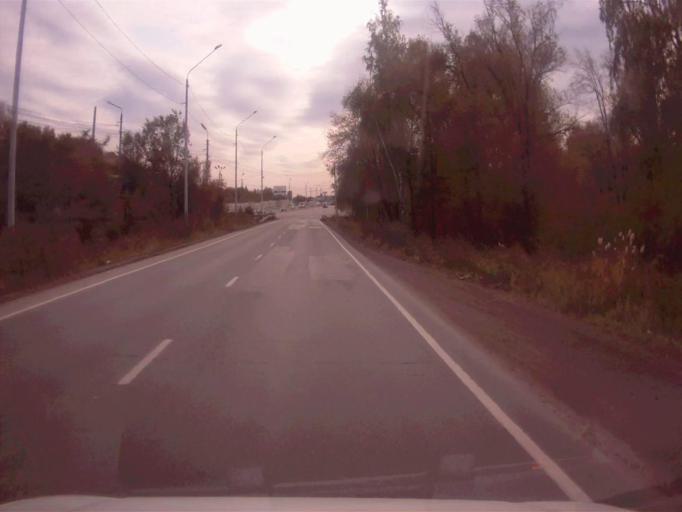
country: RU
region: Chelyabinsk
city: Novosineglazovskiy
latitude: 55.0786
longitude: 61.3881
